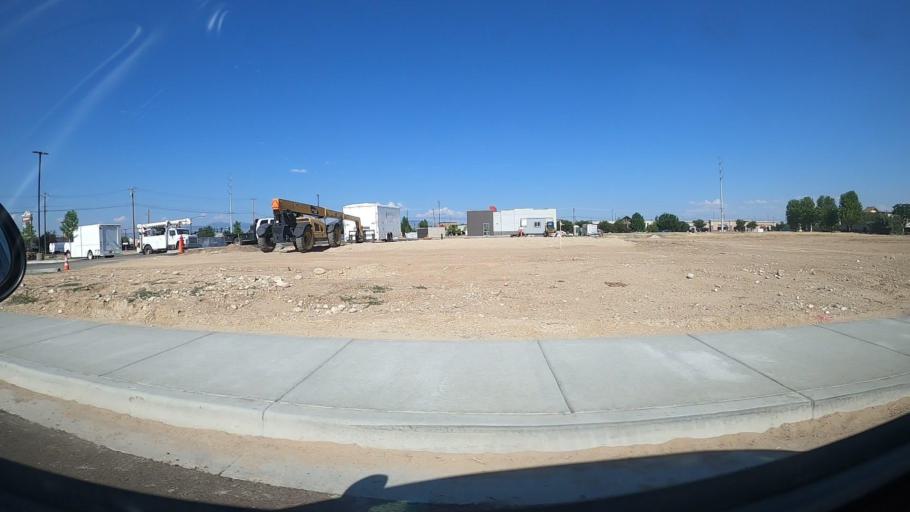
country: US
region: Idaho
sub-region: Ada County
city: Meridian
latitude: 43.6329
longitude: -116.3565
